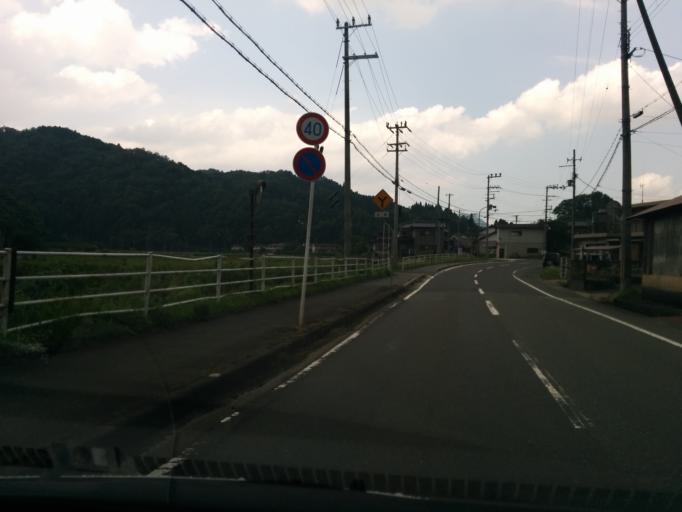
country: JP
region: Kyoto
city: Fukuchiyama
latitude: 35.4001
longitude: 135.1484
